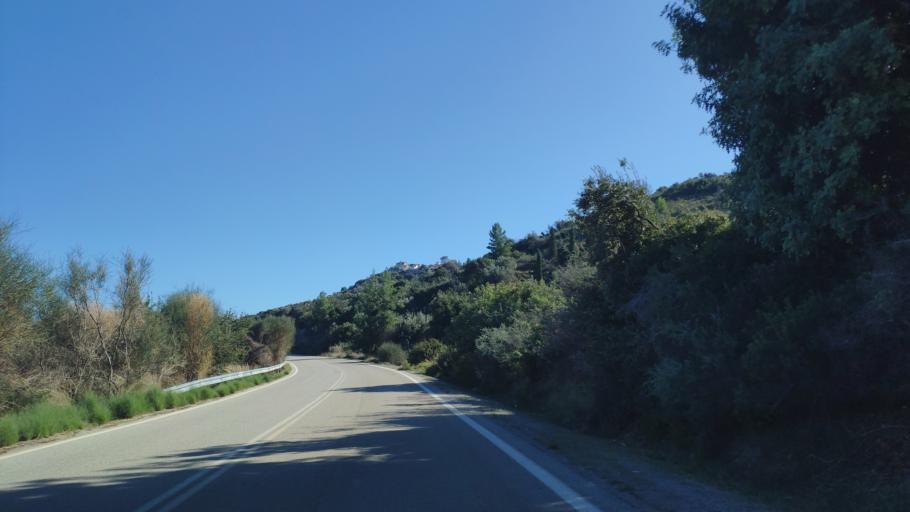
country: GR
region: Peloponnese
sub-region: Nomos Argolidos
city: Palaia Epidavros
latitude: 37.5801
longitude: 23.2354
